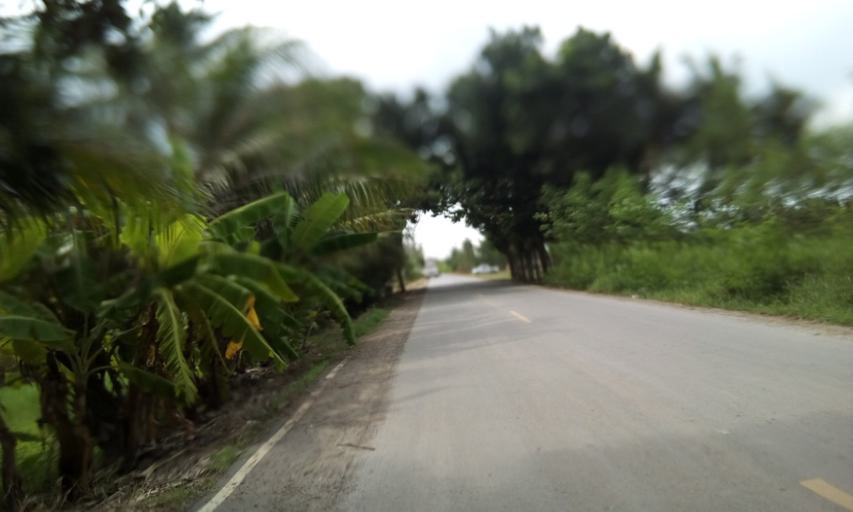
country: TH
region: Pathum Thani
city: Ban Lam Luk Ka
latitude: 14.0204
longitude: 100.8467
